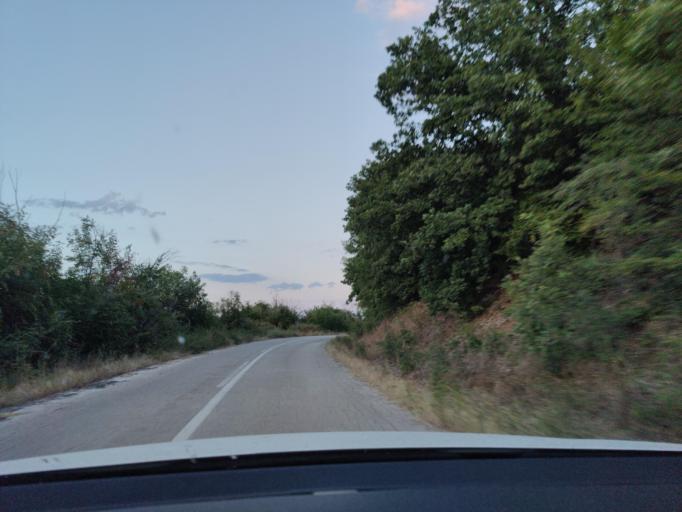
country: GR
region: Central Macedonia
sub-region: Nomos Serron
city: Chrysochorafa
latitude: 41.1804
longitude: 23.1454
